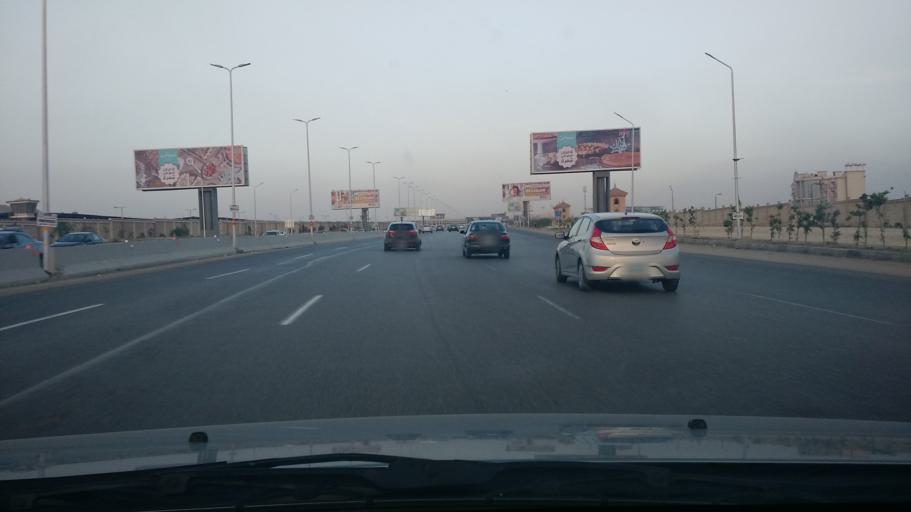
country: EG
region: Muhafazat al Qahirah
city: Cairo
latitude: 30.0246
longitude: 31.3614
